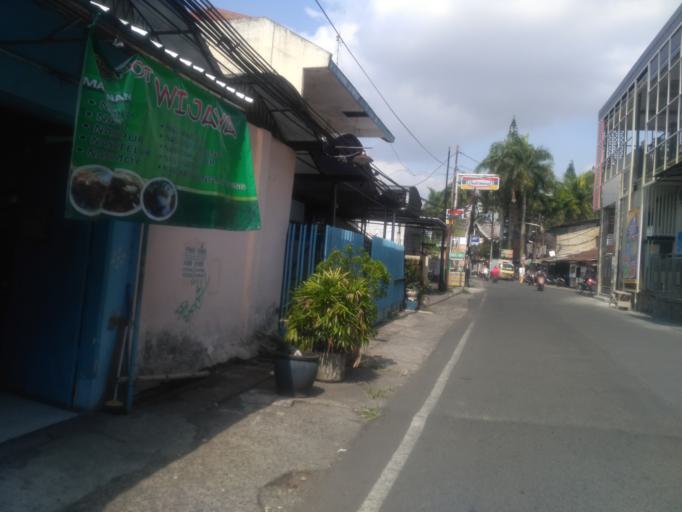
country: ID
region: East Java
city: Malang
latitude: -7.9412
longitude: 112.6385
